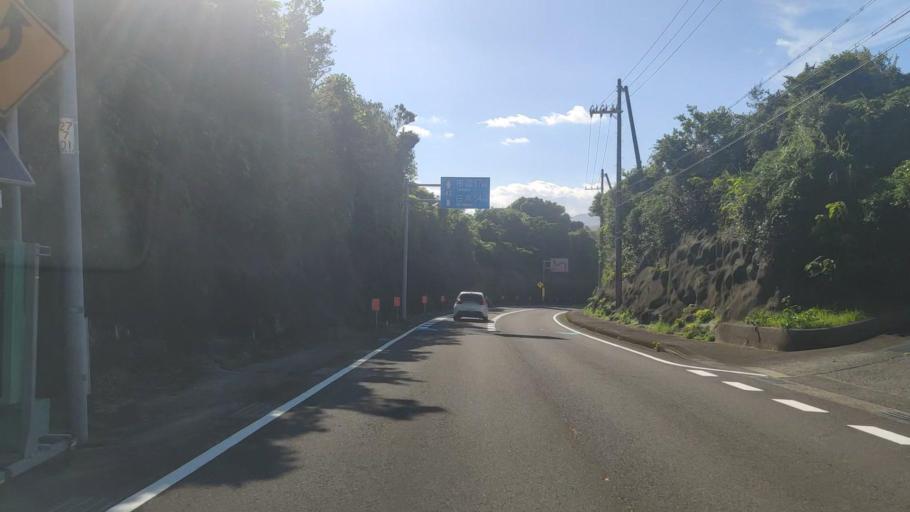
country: JP
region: Wakayama
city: Tanabe
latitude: 33.5019
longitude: 135.6482
